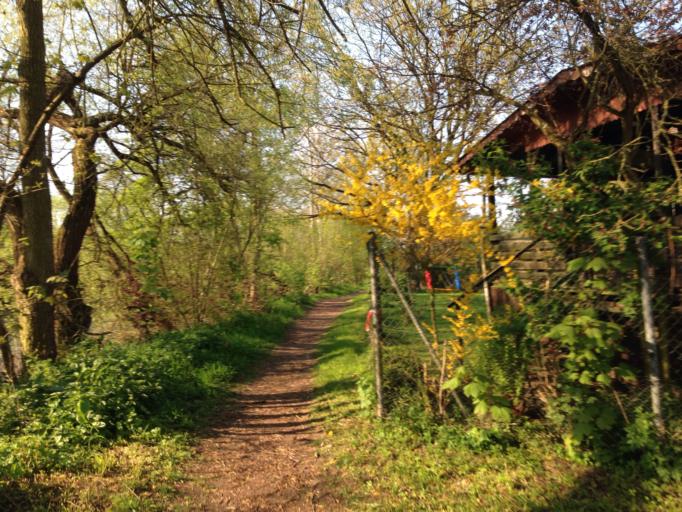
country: DE
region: Hesse
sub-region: Regierungsbezirk Giessen
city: Giessen
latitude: 50.6107
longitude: 8.6672
